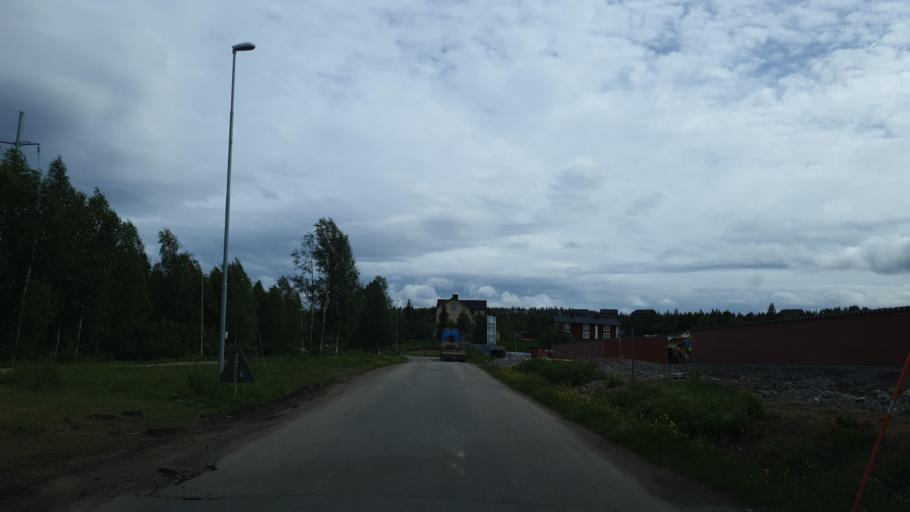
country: SE
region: Norrbotten
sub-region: Gallivare Kommun
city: Gaellivare
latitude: 67.1292
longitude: 20.6483
